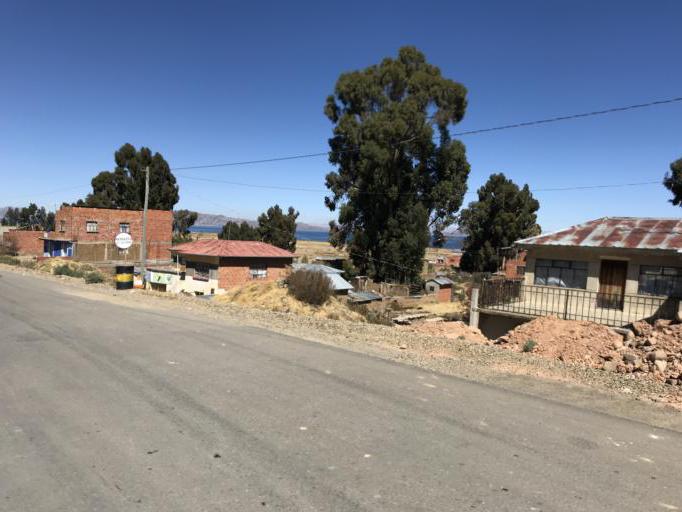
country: BO
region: La Paz
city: Huatajata
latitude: -16.1993
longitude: -68.7140
